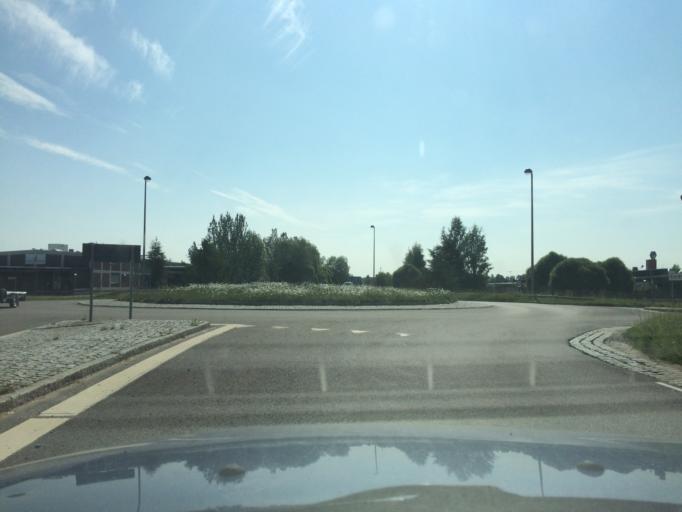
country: SE
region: Norrbotten
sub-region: Pitea Kommun
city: Bergsviken
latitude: 65.3462
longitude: 21.4052
